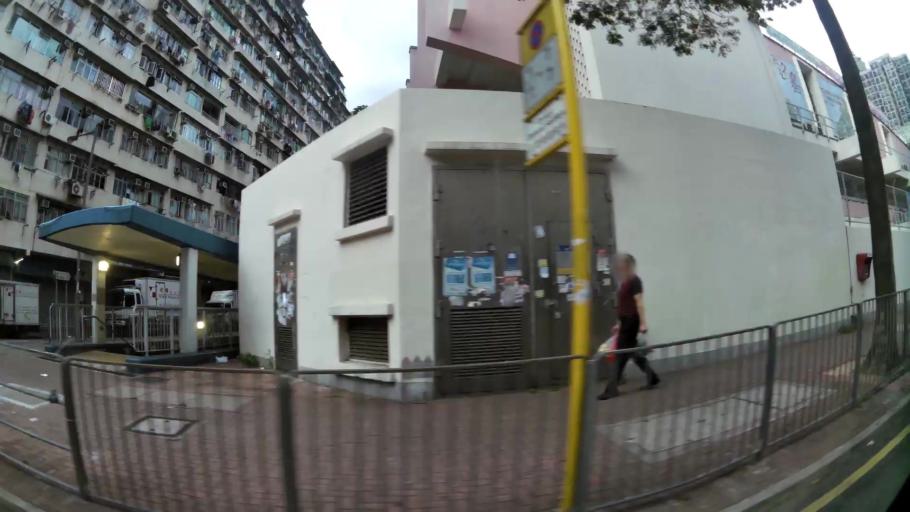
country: HK
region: Sham Shui Po
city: Sham Shui Po
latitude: 22.3188
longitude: 114.1640
